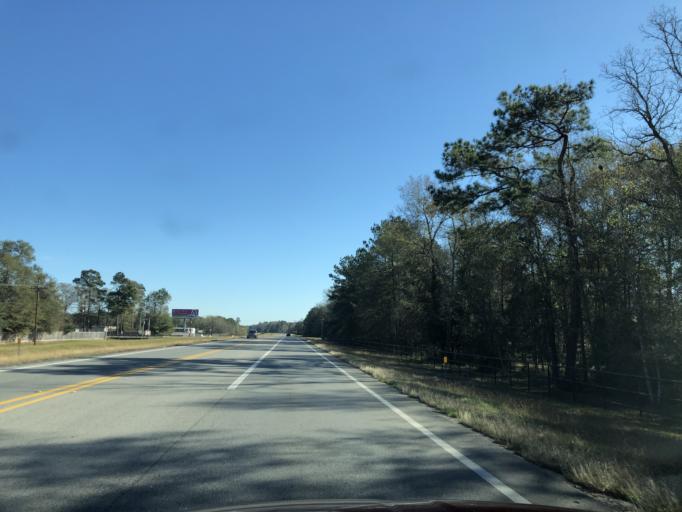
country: US
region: Texas
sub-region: Montgomery County
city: Porter Heights
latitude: 30.2138
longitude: -95.3183
